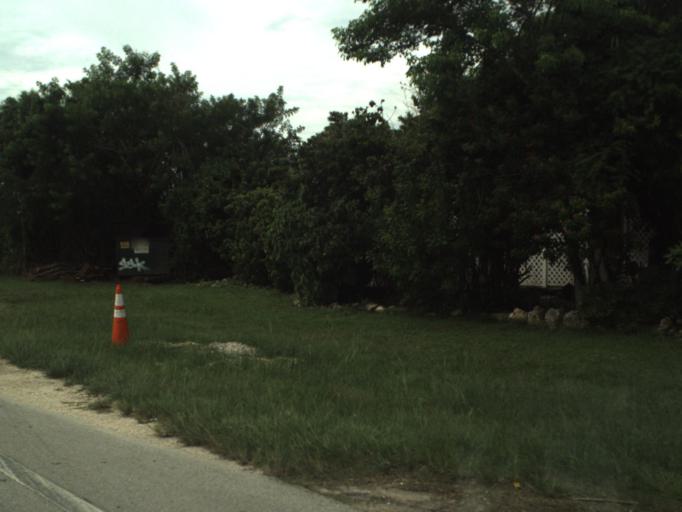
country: US
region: Florida
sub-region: Miami-Dade County
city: Naranja
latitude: 25.5563
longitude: -80.4782
